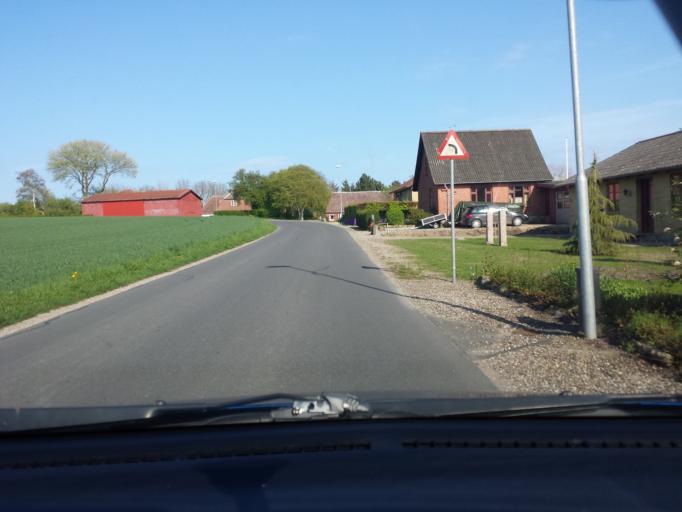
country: DK
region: South Denmark
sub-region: Langeland Kommune
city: Rudkobing
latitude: 54.9025
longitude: 10.7644
